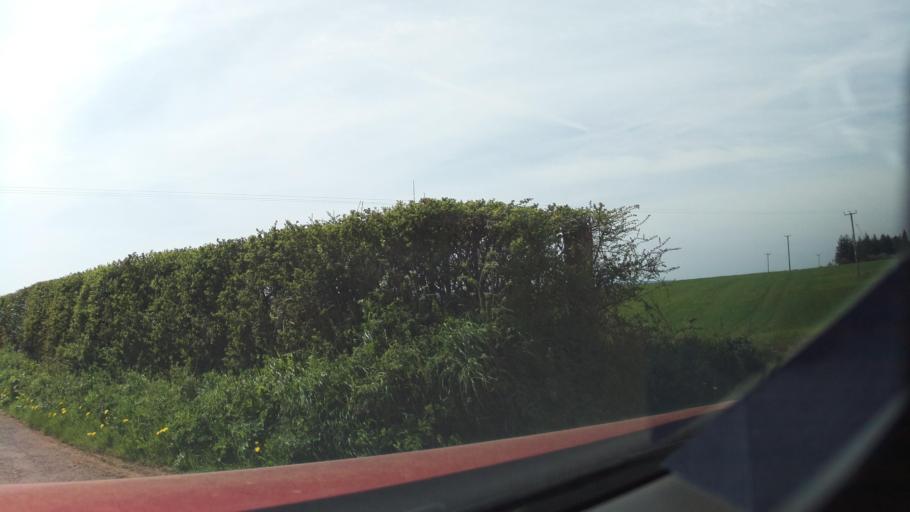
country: GB
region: England
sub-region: Dorset
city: Sherborne
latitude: 50.9643
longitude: -2.5191
